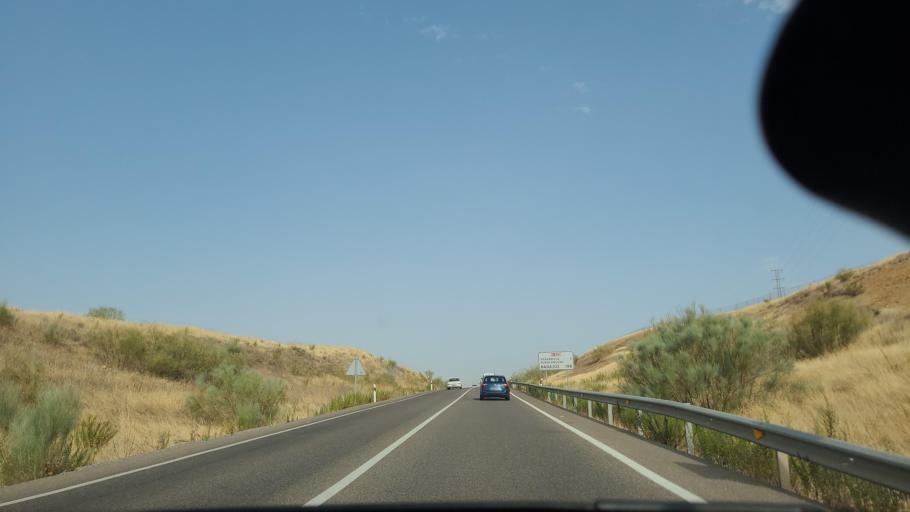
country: ES
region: Andalusia
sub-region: Province of Cordoba
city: Belmez
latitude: 38.2787
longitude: -5.2037
